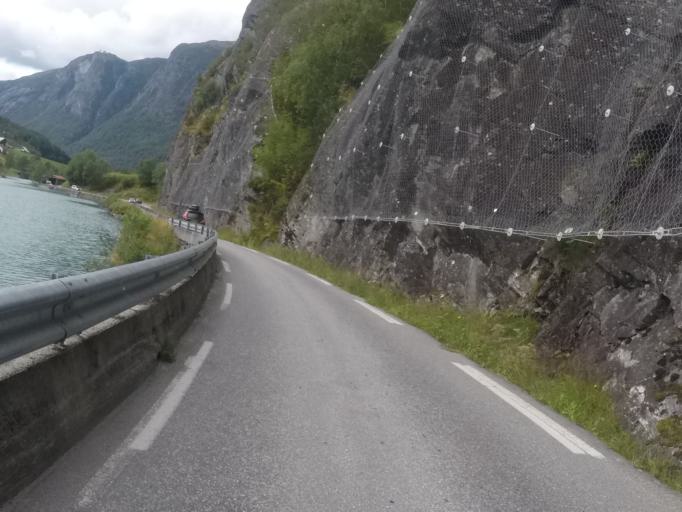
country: NO
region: Sogn og Fjordane
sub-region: Stryn
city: Stryn
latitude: 61.8579
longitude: 6.8948
